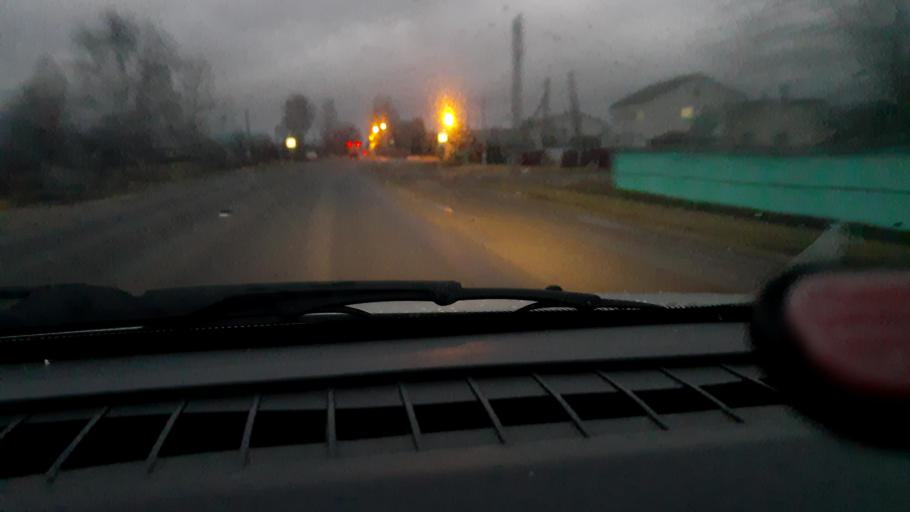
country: RU
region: Nizjnij Novgorod
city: Uren'
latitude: 57.4455
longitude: 45.7324
